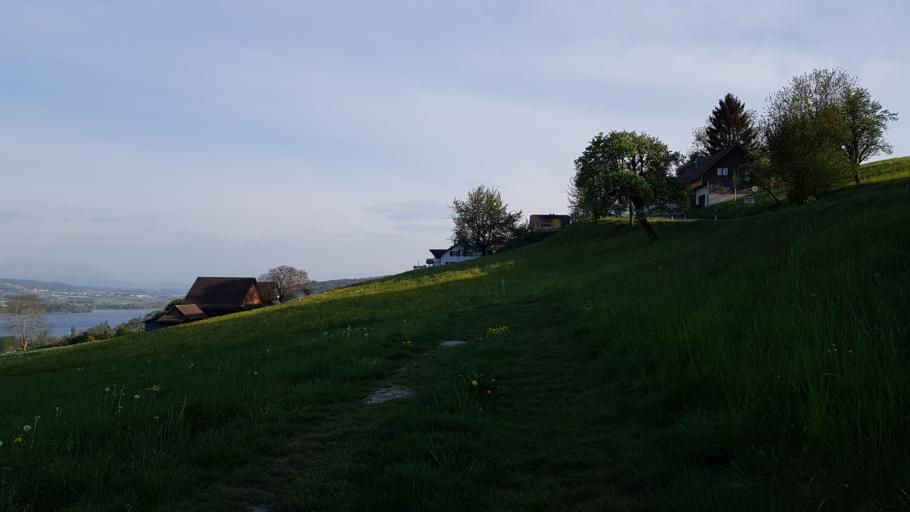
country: CH
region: Aargau
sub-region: Bezirk Kulm
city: Reinach
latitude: 47.2793
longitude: 8.1972
